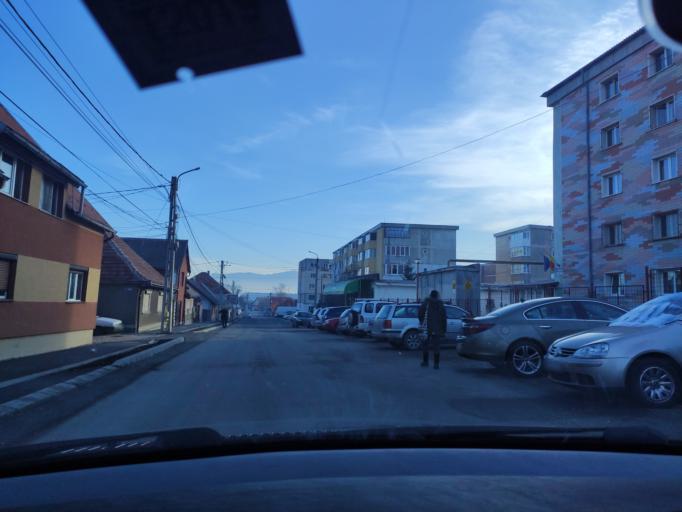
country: RO
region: Brasov
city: Codlea
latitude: 45.6911
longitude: 25.4403
